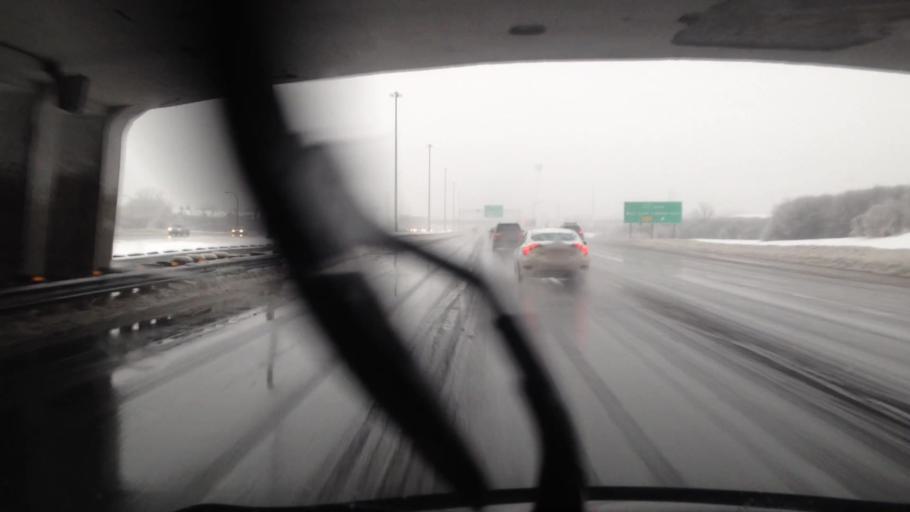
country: CA
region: Quebec
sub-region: Laurentides
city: Rosemere
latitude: 45.5857
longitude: -73.7876
